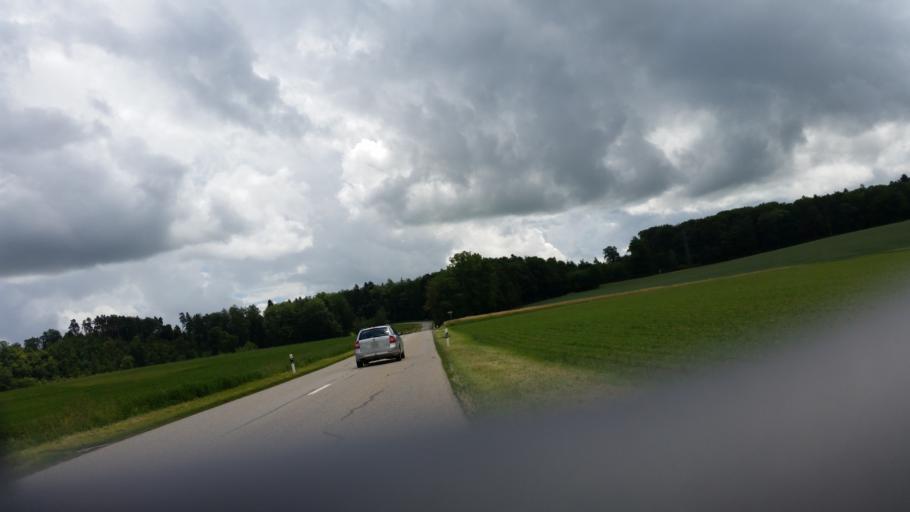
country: CH
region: Vaud
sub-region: Jura-Nord vaudois District
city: Yverdon-les-Bains
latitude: 46.7545
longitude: 6.6783
